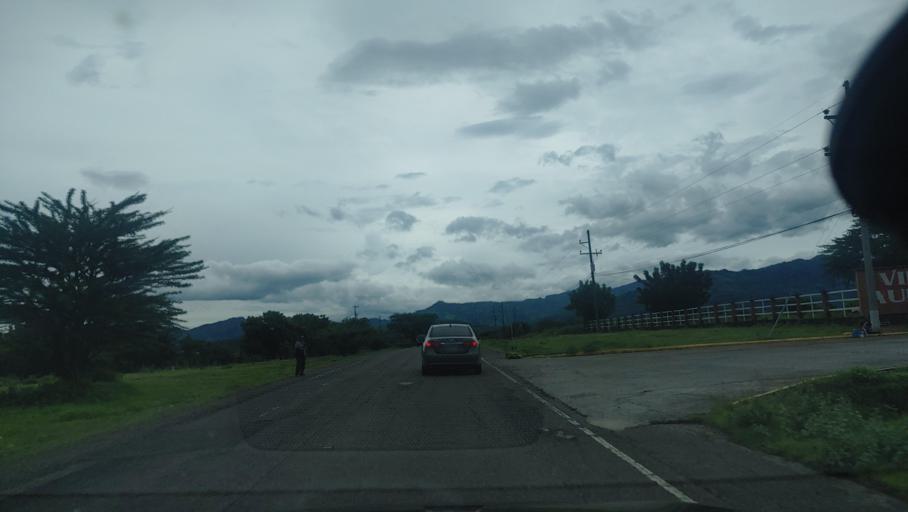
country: HN
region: Choluteca
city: Santa Ana de Yusguare
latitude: 13.3437
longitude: -87.1213
